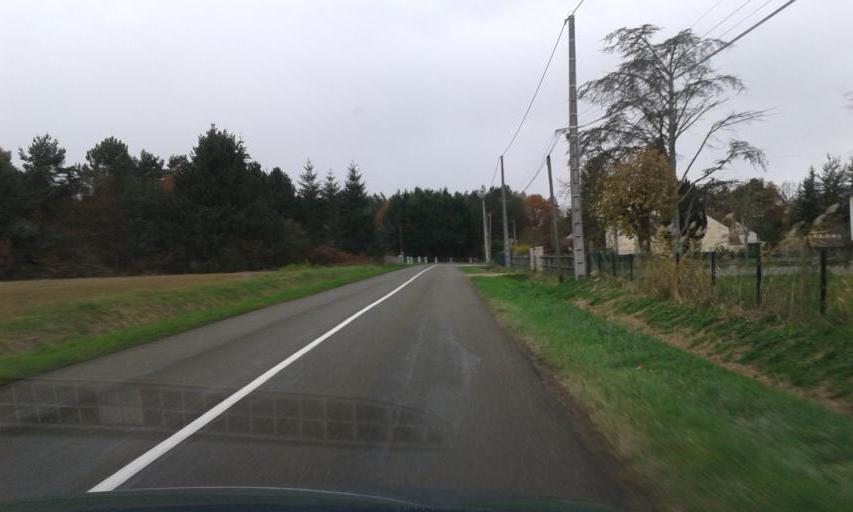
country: FR
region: Centre
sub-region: Departement du Loiret
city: Vitry-aux-Loges
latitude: 47.9312
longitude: 2.2263
